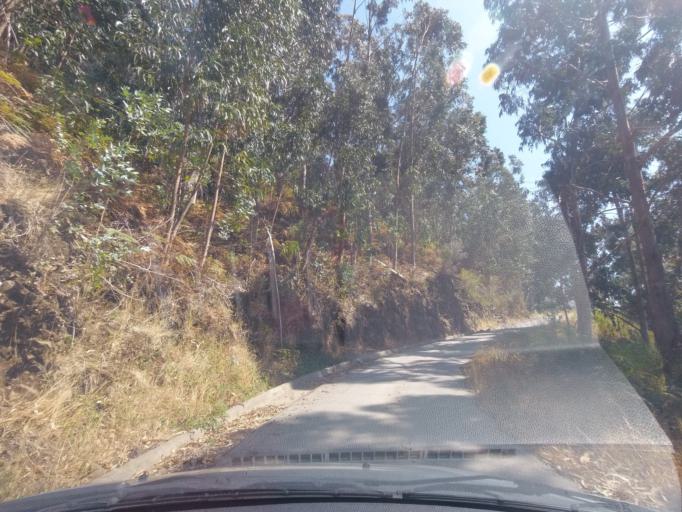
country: PT
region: Madeira
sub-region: Sao Vicente
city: Sao Vicente
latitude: 32.7410
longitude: -17.0284
